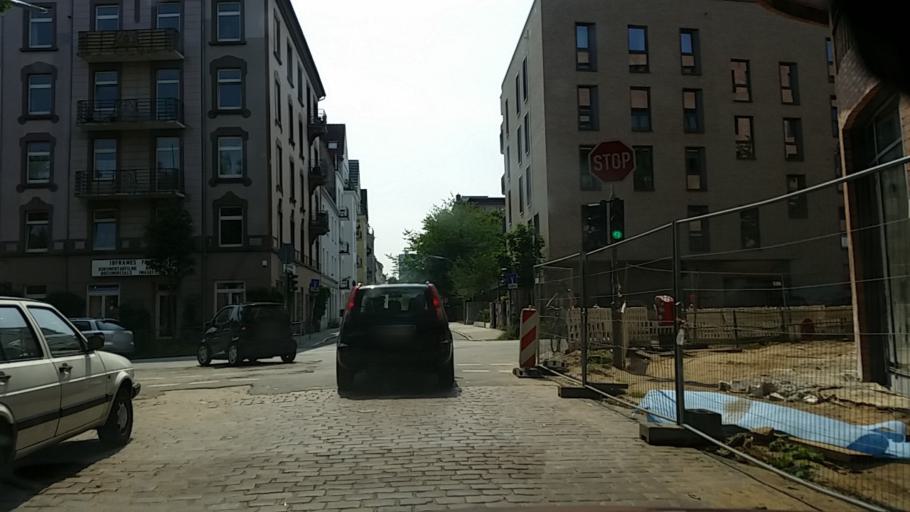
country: DE
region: Hamburg
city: Altona
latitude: 53.5575
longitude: 9.9325
